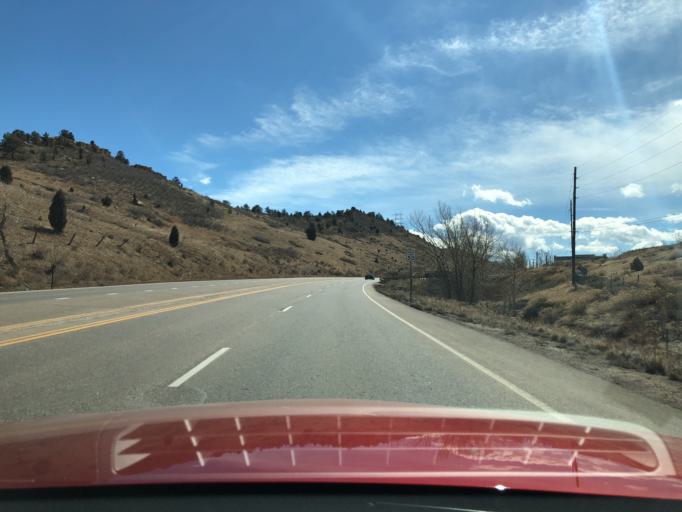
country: US
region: Colorado
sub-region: Jefferson County
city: West Pleasant View
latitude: 39.7118
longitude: -105.2056
